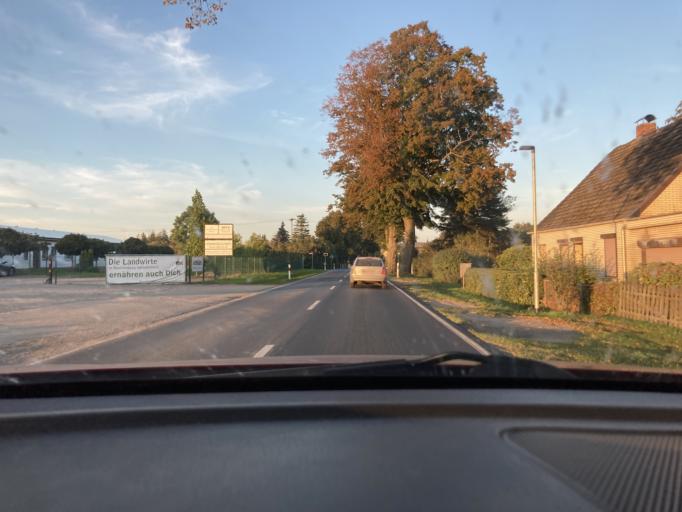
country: DE
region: Mecklenburg-Vorpommern
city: Alt-Sanitz
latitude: 53.7548
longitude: 13.6283
